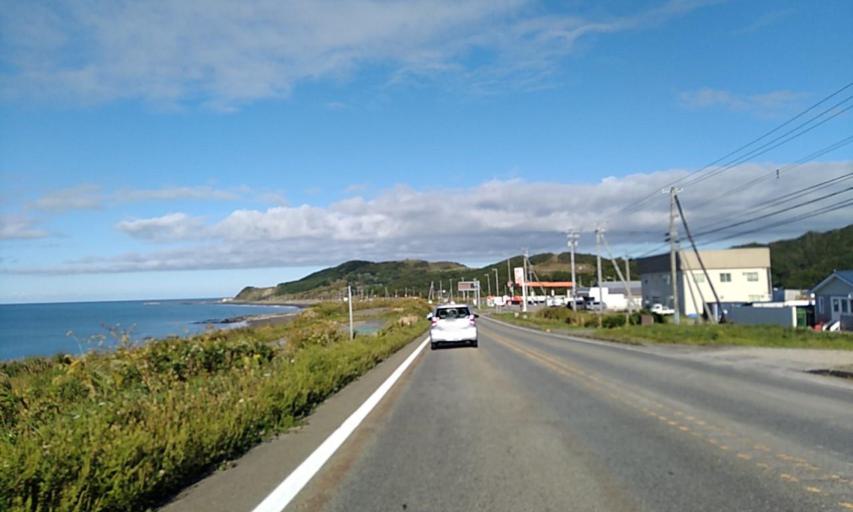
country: JP
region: Hokkaido
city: Shizunai-furukawacho
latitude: 42.1843
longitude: 142.7252
